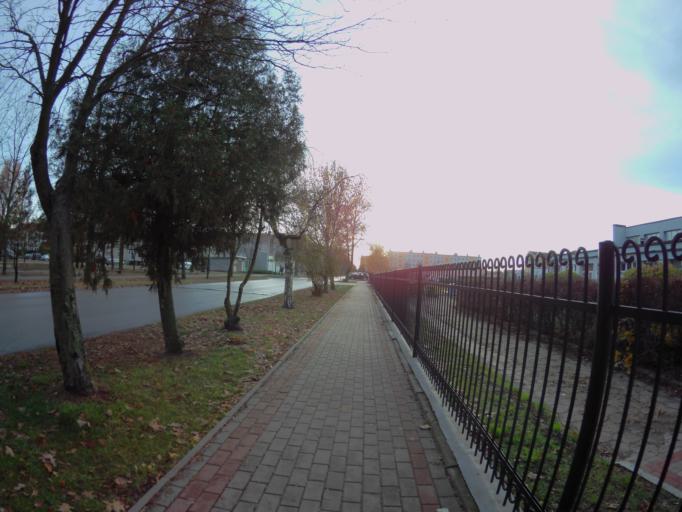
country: PL
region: Subcarpathian Voivodeship
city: Nowa Sarzyna
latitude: 50.3188
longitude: 22.3427
